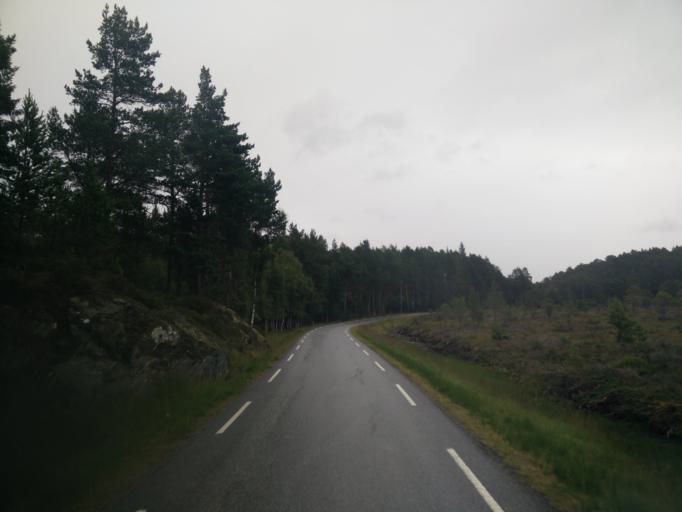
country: NO
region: More og Romsdal
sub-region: Kristiansund
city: Rensvik
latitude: 63.0395
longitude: 7.9397
